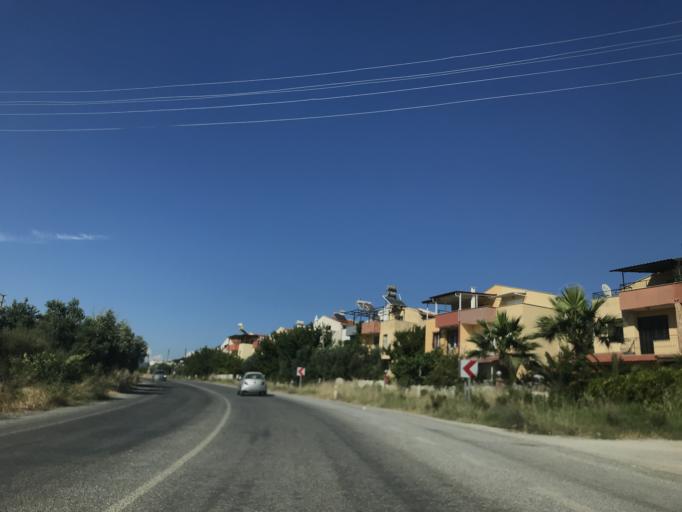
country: TR
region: Aydin
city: Davutlar
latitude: 37.7219
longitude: 27.2547
